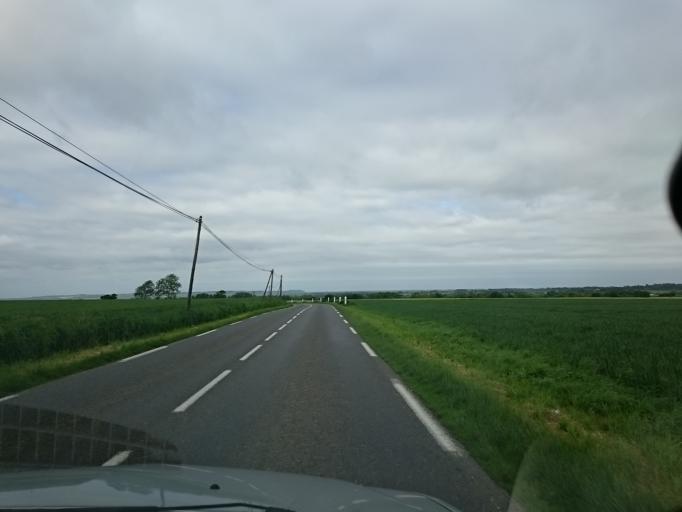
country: FR
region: Lower Normandy
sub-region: Departement de la Manche
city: Pontorson
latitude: 48.5561
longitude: -1.4479
